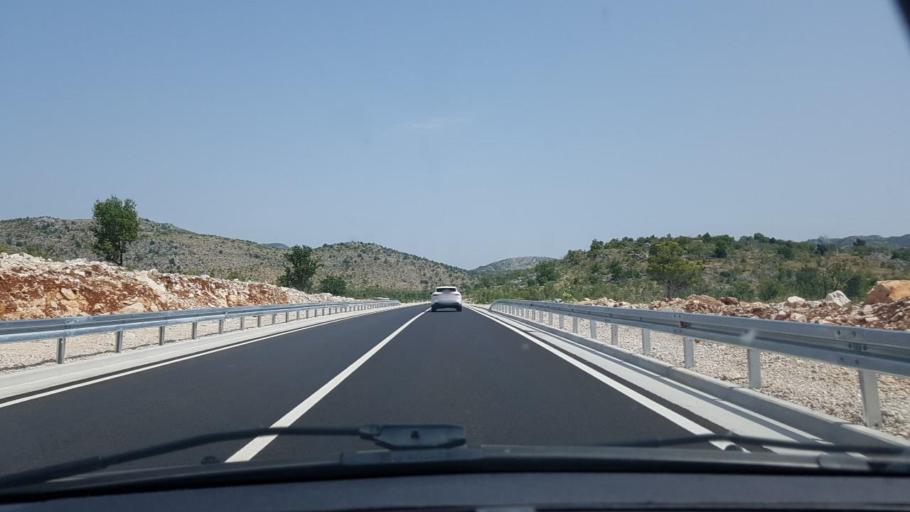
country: HR
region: Dubrovacko-Neretvanska
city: Podgora
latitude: 42.9465
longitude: 17.7672
